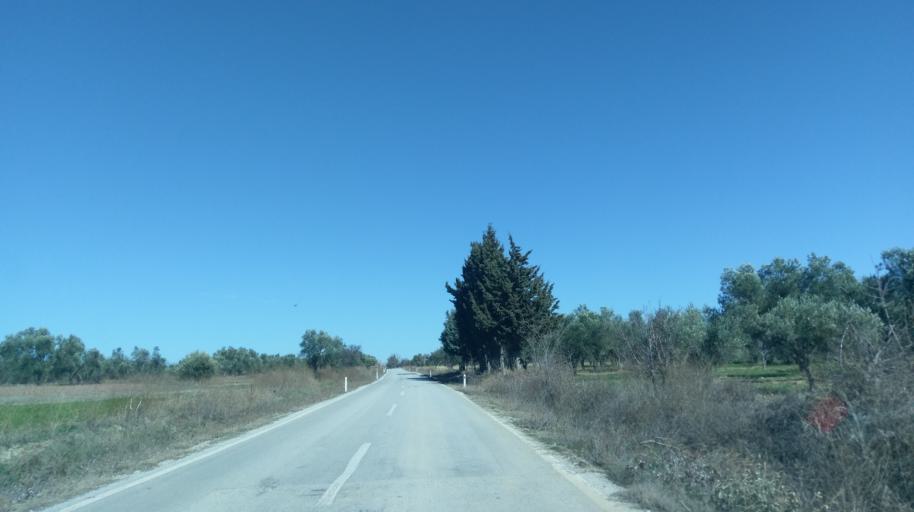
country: TR
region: Canakkale
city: Intepe
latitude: 40.0802
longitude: 26.2190
